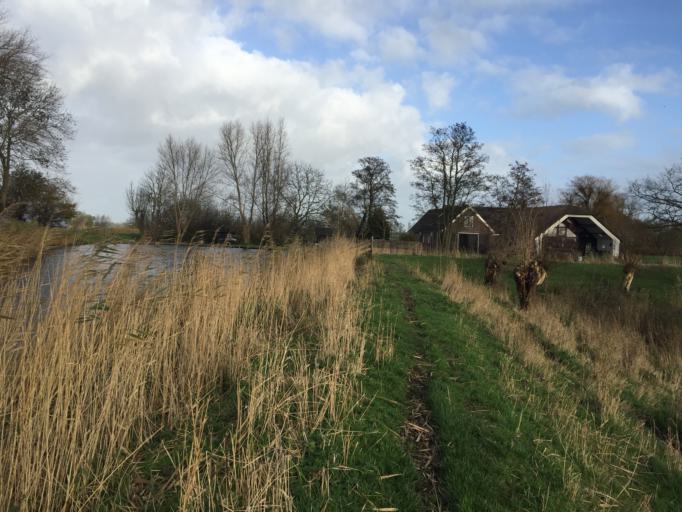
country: NL
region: North Holland
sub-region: Gemeente Ouder-Amstel
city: Ouderkerk aan de Amstel
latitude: 52.2597
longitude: 4.9422
